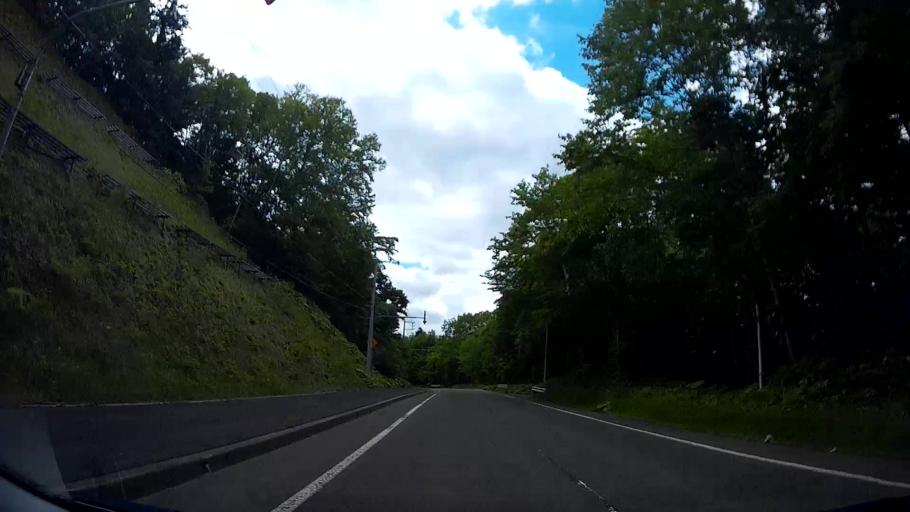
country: JP
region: Hokkaido
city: Kitahiroshima
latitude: 42.8437
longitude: 141.4424
